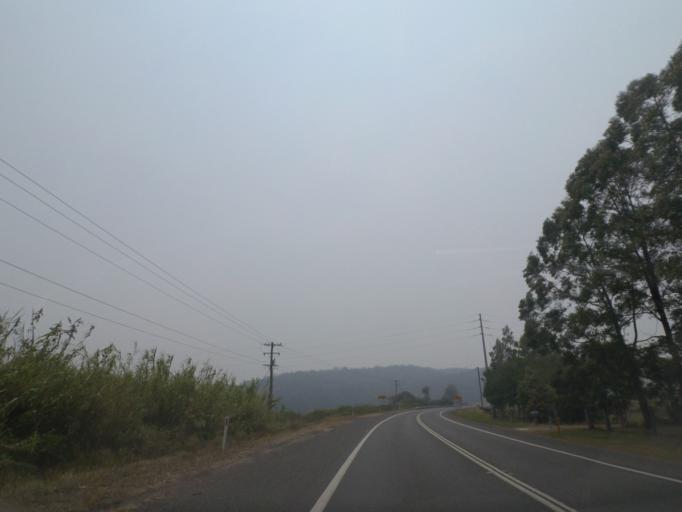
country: AU
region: New South Wales
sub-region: Clarence Valley
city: Maclean
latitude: -29.5439
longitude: 153.1561
